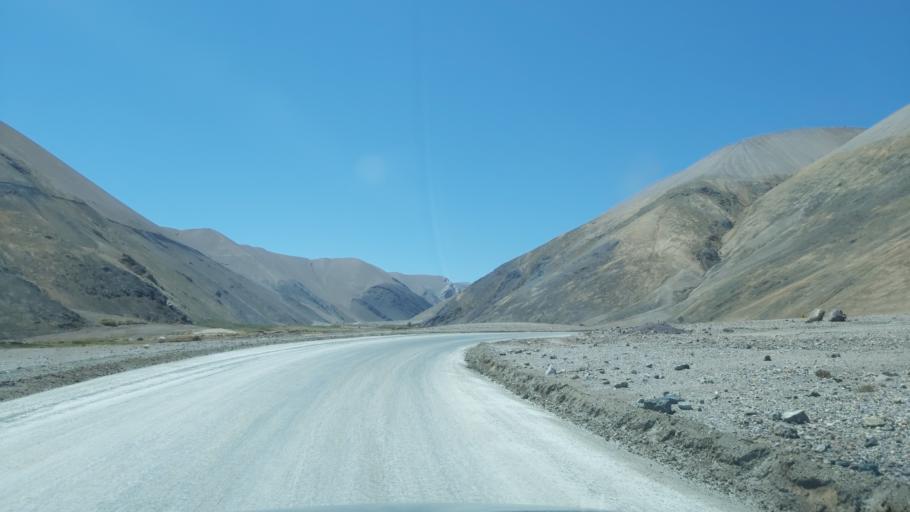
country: CL
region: Atacama
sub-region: Provincia de Chanaral
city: Diego de Almagro
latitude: -26.3961
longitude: -69.5135
